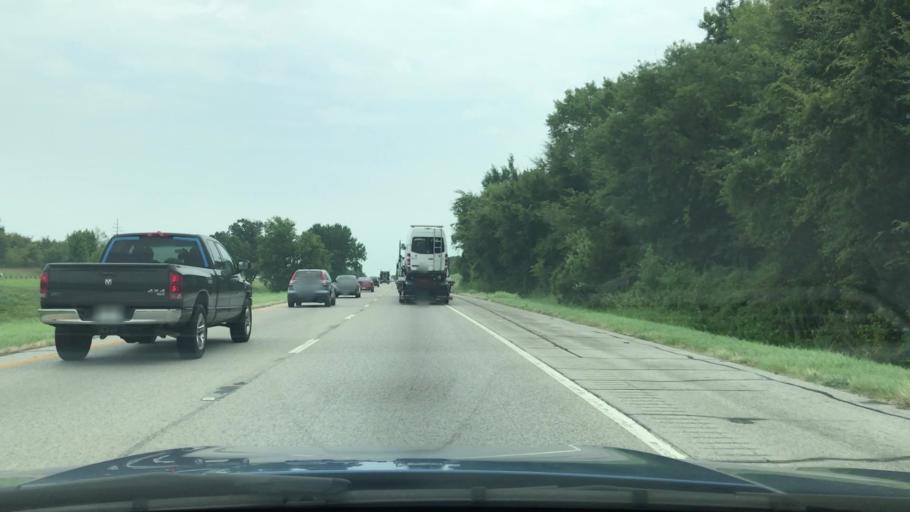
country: US
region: Texas
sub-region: Smith County
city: Hideaway
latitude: 32.4801
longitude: -95.4965
